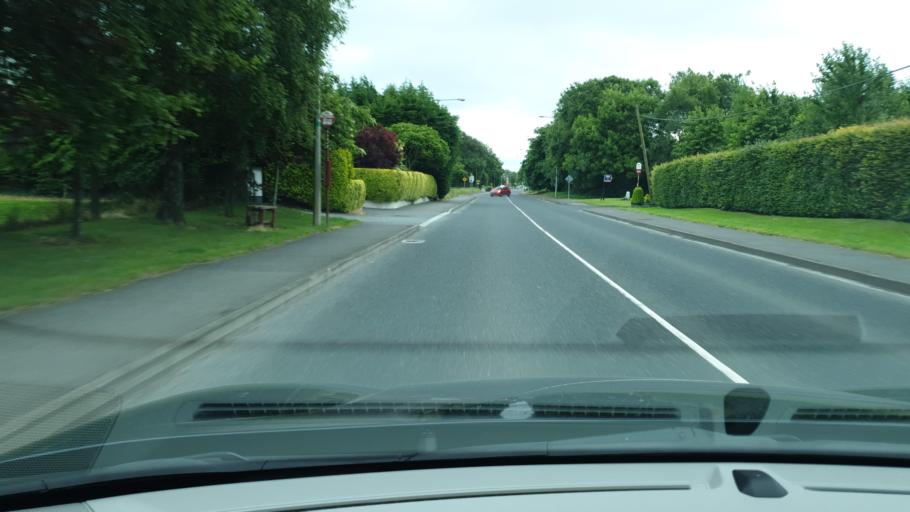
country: IE
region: Leinster
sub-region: An Mhi
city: Dunshaughlin
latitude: 53.4715
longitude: -6.5397
